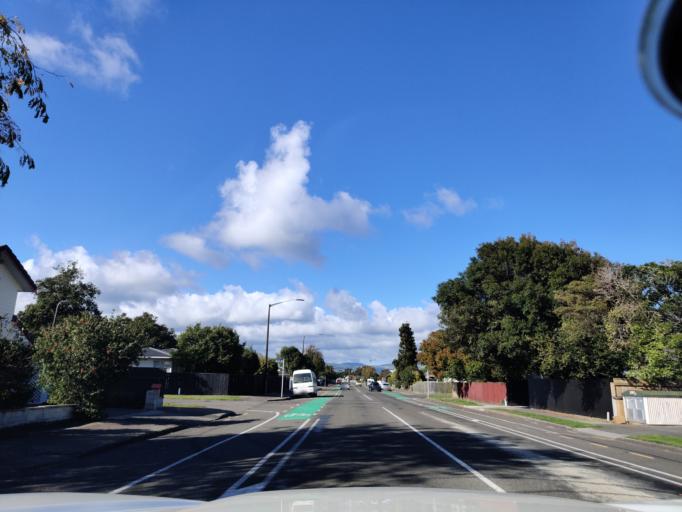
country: NZ
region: Manawatu-Wanganui
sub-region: Palmerston North City
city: Palmerston North
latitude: -40.3498
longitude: 175.5973
